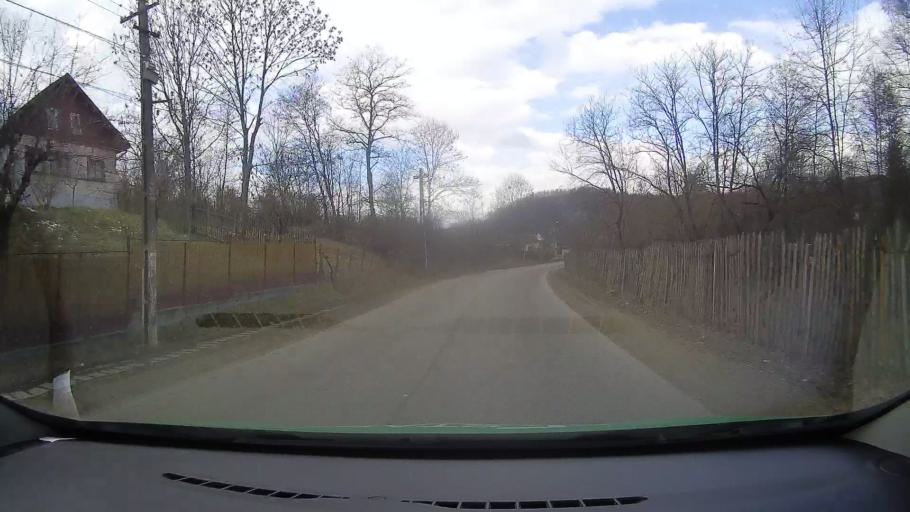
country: RO
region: Dambovita
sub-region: Comuna Visinesti
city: Visinesti
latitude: 45.0656
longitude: 25.5518
